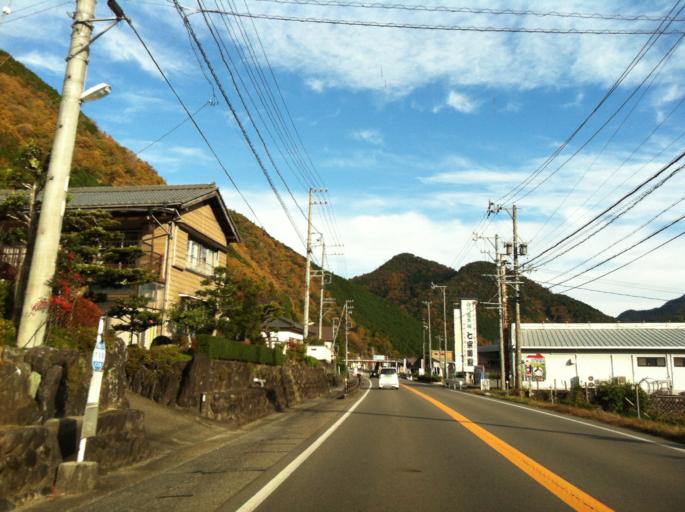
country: JP
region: Gifu
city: Minokamo
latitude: 35.5314
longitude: 137.1145
